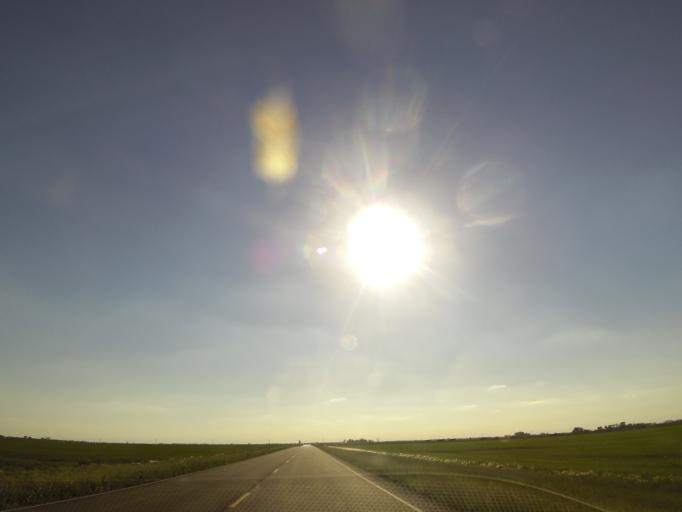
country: US
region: North Dakota
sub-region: Grand Forks County
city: Grand Forks Air Force Base
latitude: 48.1358
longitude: -97.2383
